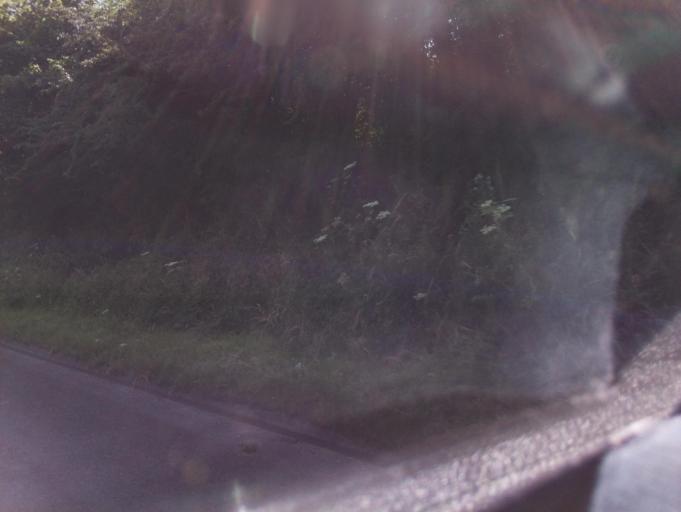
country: GB
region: Wales
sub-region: Caerphilly County Borough
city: Hengoed
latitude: 51.6512
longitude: -3.2229
